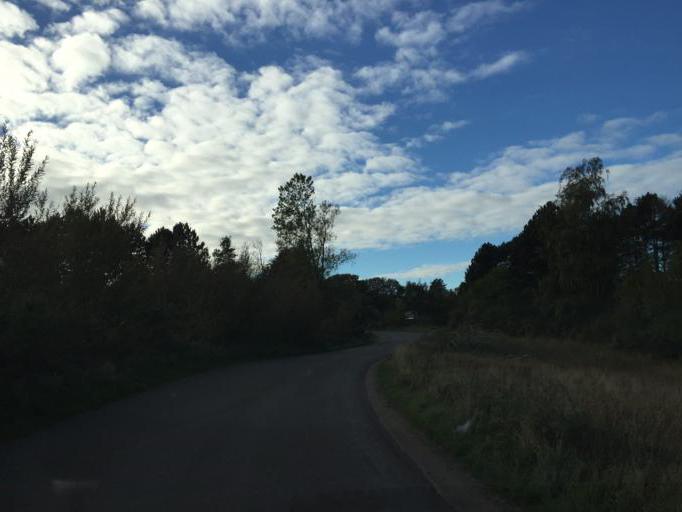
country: DK
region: Zealand
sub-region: Odsherred Kommune
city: Asnaes
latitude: 55.8419
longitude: 11.4703
